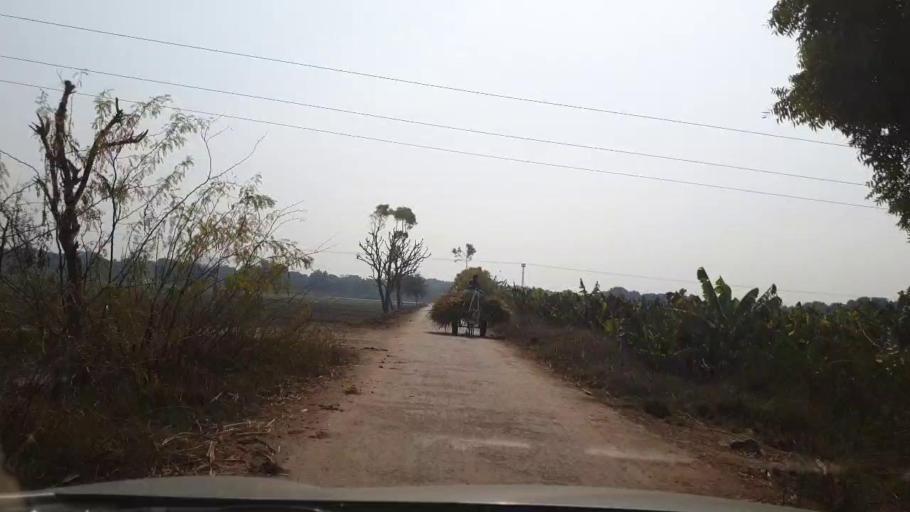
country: PK
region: Sindh
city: Tando Allahyar
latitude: 25.4876
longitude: 68.7689
